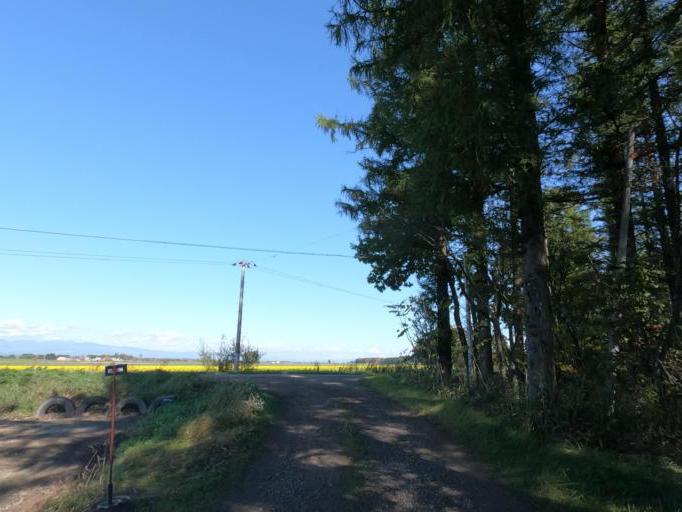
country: JP
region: Hokkaido
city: Otofuke
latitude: 43.0169
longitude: 143.2701
